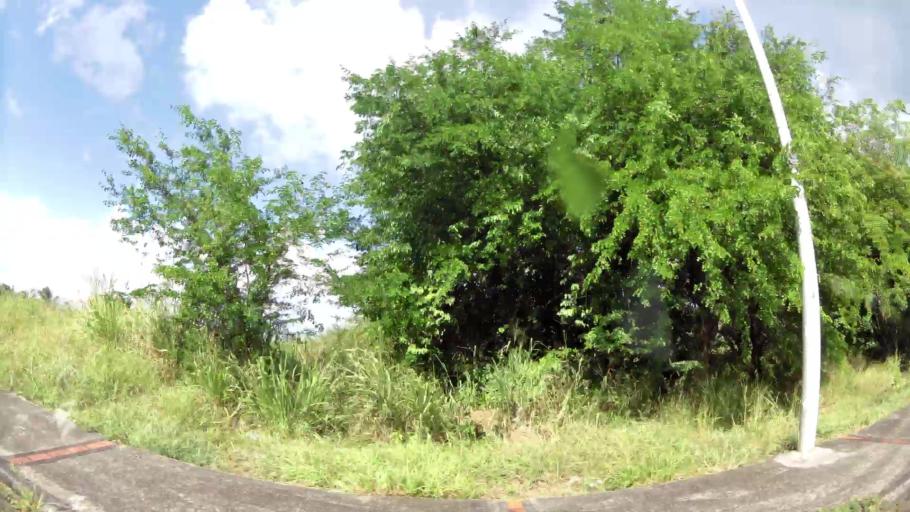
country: MQ
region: Martinique
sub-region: Martinique
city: Les Trois-Ilets
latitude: 14.5345
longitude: -61.0315
